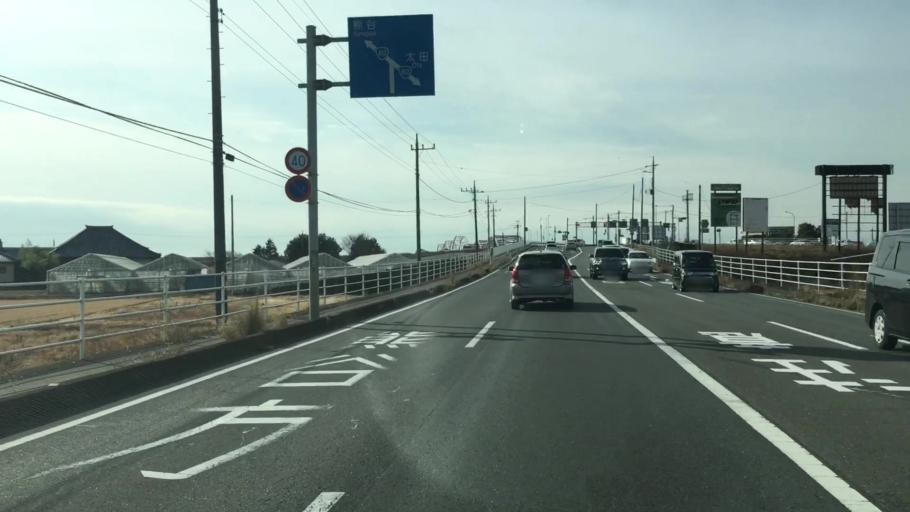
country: JP
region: Saitama
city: Menuma
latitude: 36.2441
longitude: 139.3827
